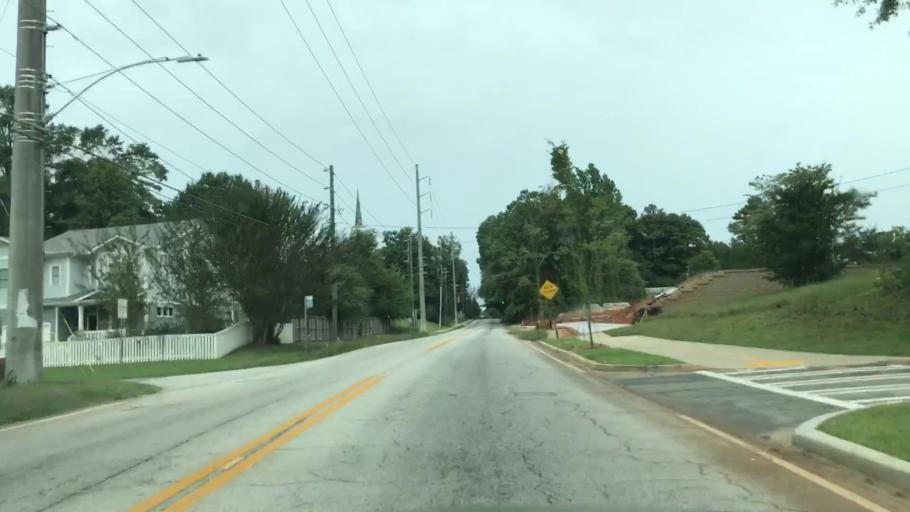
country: US
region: Georgia
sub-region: DeKalb County
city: Belvedere Park
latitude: 33.7615
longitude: -84.2776
